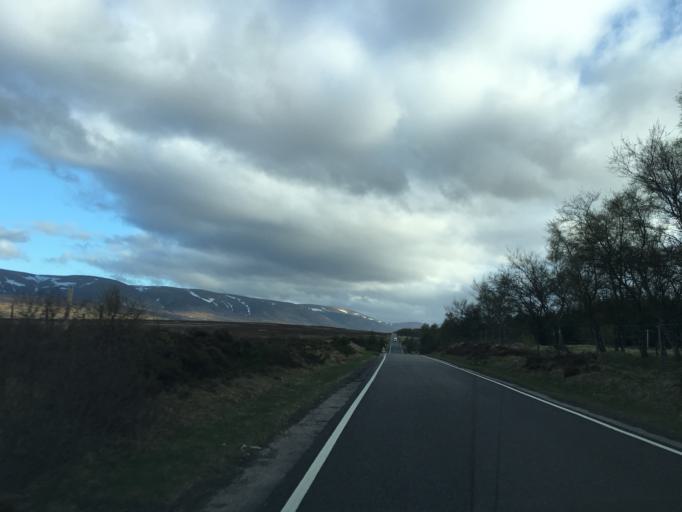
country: GB
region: Scotland
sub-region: Highland
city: Kingussie
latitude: 56.9599
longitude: -4.2447
